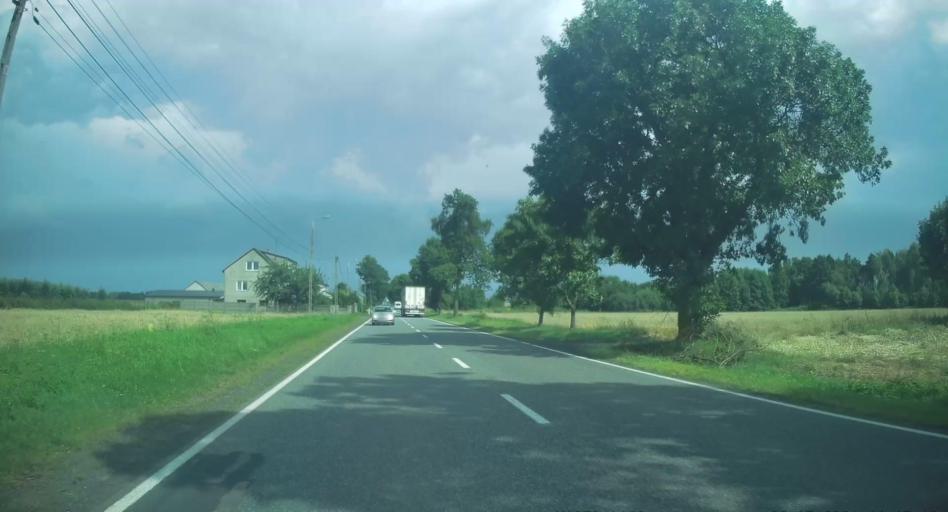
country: PL
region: Lodz Voivodeship
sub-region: Powiat brzezinski
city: Jezow
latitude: 51.8116
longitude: 19.9851
